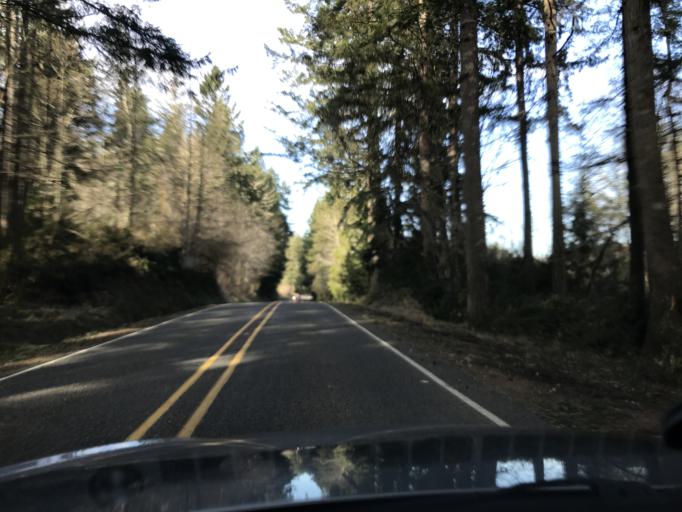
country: US
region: Washington
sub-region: Pierce County
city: Longbranch
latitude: 47.2330
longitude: -122.7895
